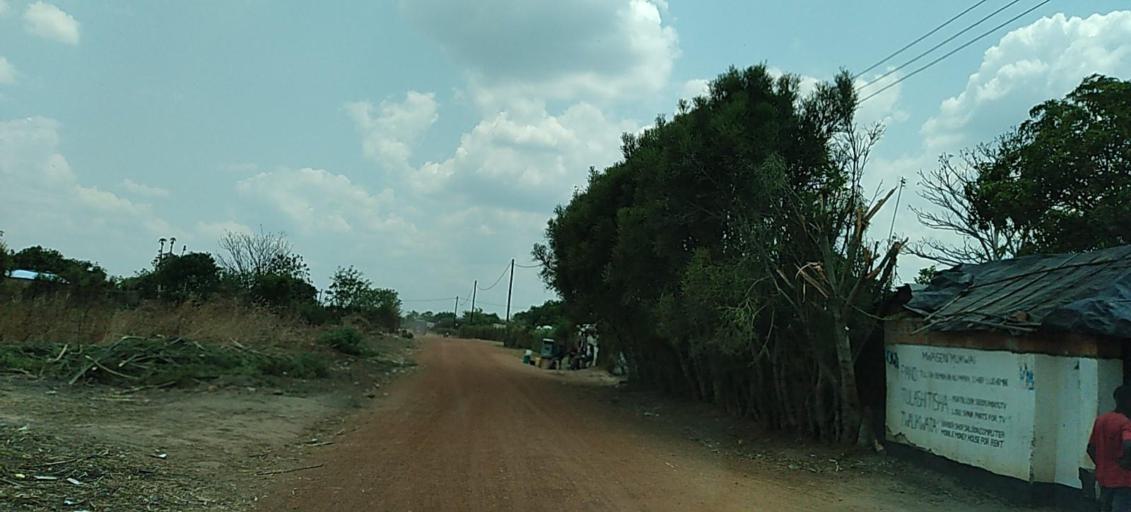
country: ZM
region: Copperbelt
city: Luanshya
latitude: -13.1231
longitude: 28.3102
